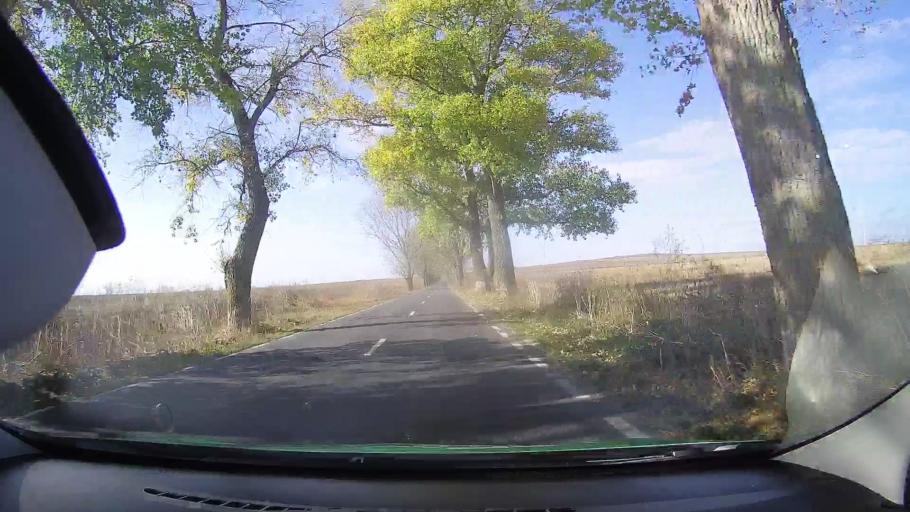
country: RO
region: Tulcea
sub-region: Comuna Valea Nucarilor
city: Iazurile
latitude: 45.0266
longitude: 29.0029
